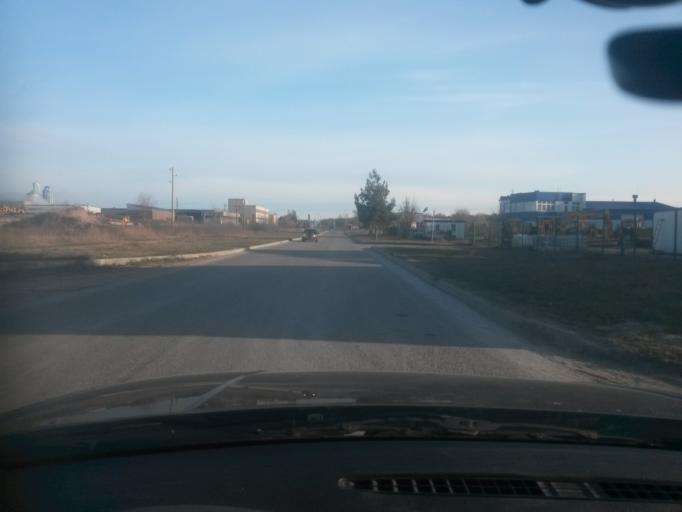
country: LV
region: Stopini
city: Ulbroka
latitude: 56.9094
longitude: 24.2460
